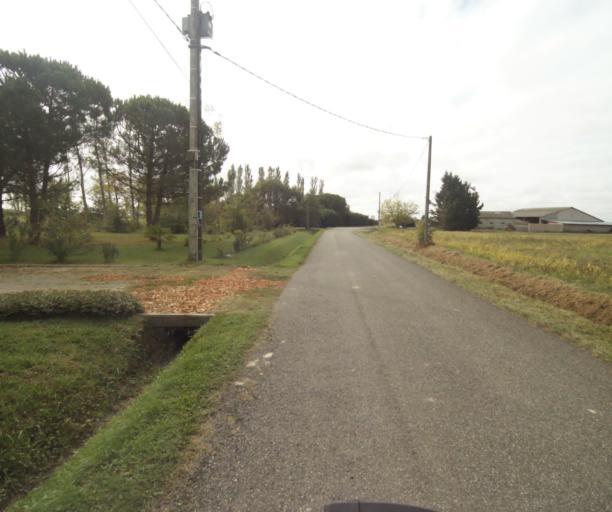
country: FR
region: Midi-Pyrenees
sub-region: Departement du Tarn-et-Garonne
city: Finhan
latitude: 43.9219
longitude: 1.2447
